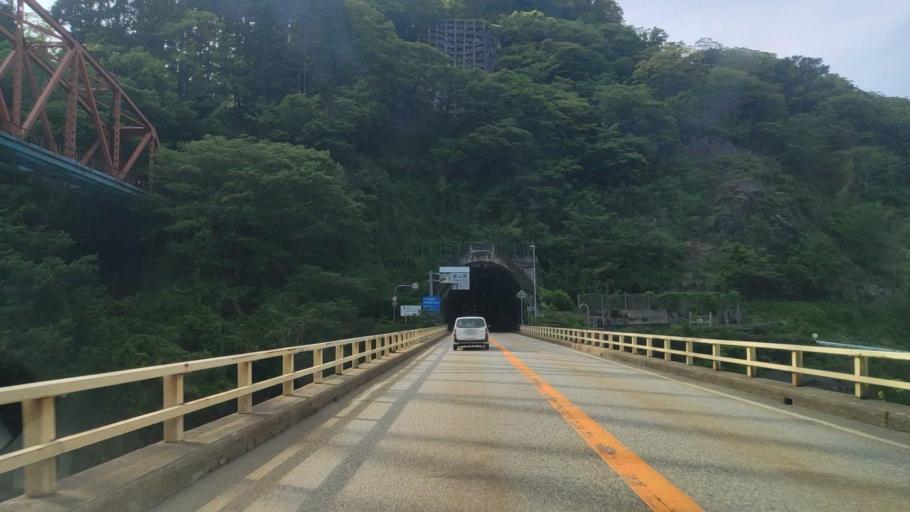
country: JP
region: Toyama
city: Yatsuomachi-higashikumisaka
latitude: 36.4613
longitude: 137.2475
